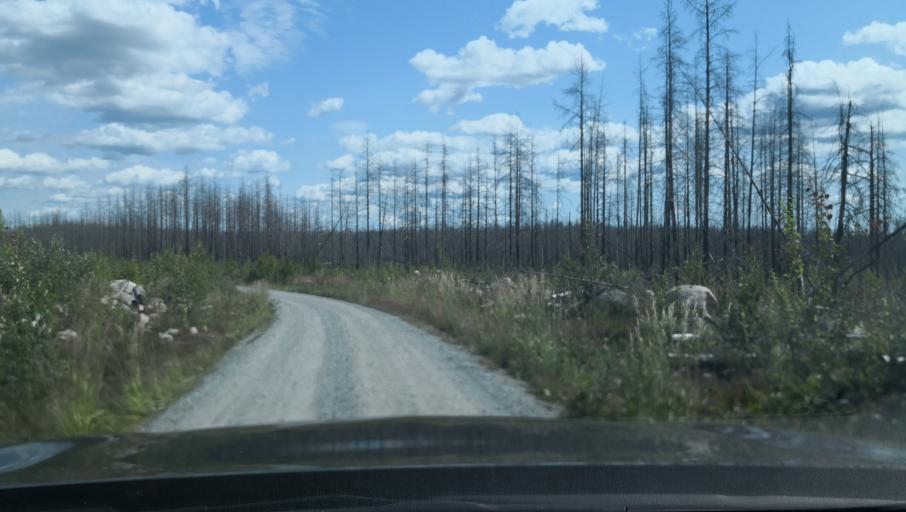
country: SE
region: Vaestmanland
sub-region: Surahammars Kommun
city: Ramnas
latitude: 59.8979
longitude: 16.1123
